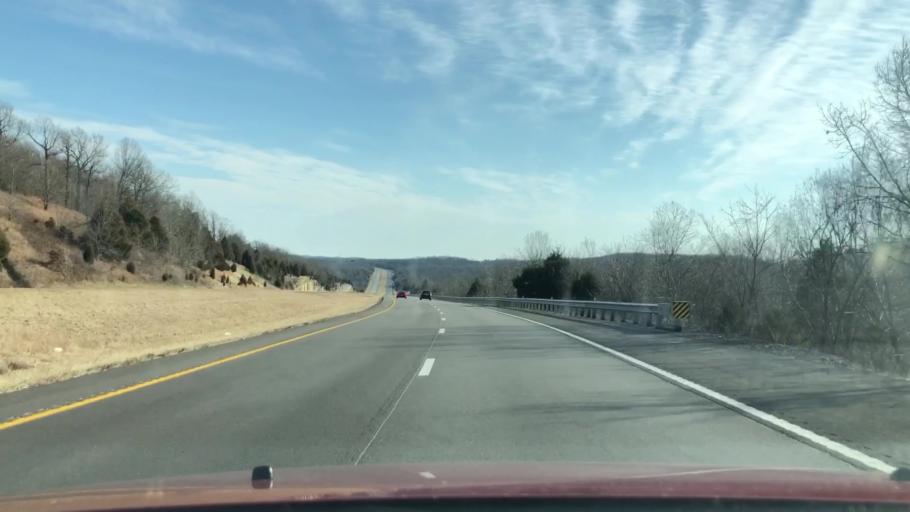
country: US
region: Missouri
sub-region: Wright County
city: Mansfield
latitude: 37.1132
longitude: -92.6694
